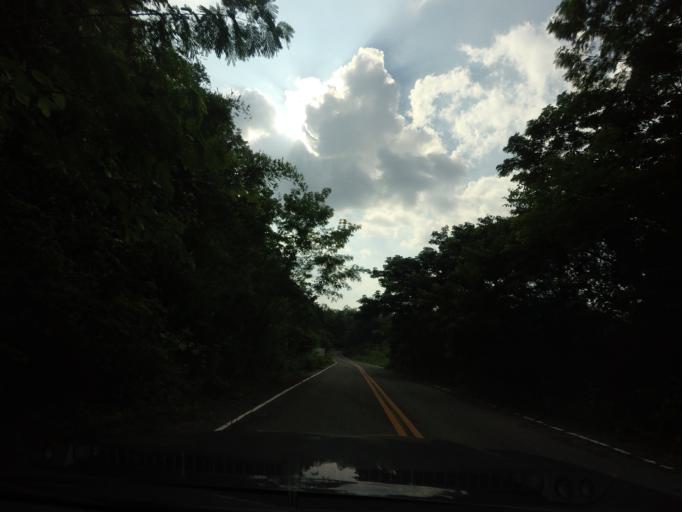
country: TH
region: Nan
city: Na Noi
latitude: 18.2902
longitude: 100.9204
